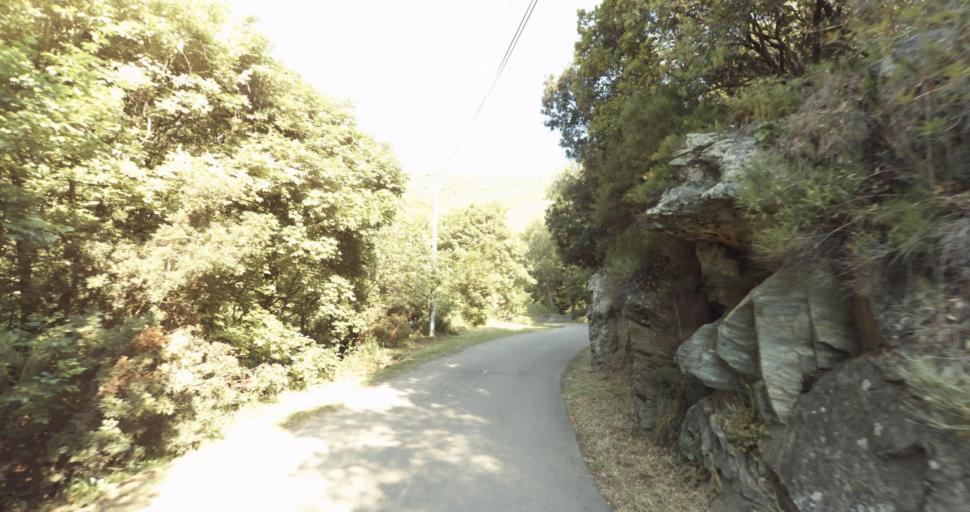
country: FR
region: Corsica
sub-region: Departement de la Haute-Corse
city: Biguglia
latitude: 42.6323
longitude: 9.4159
